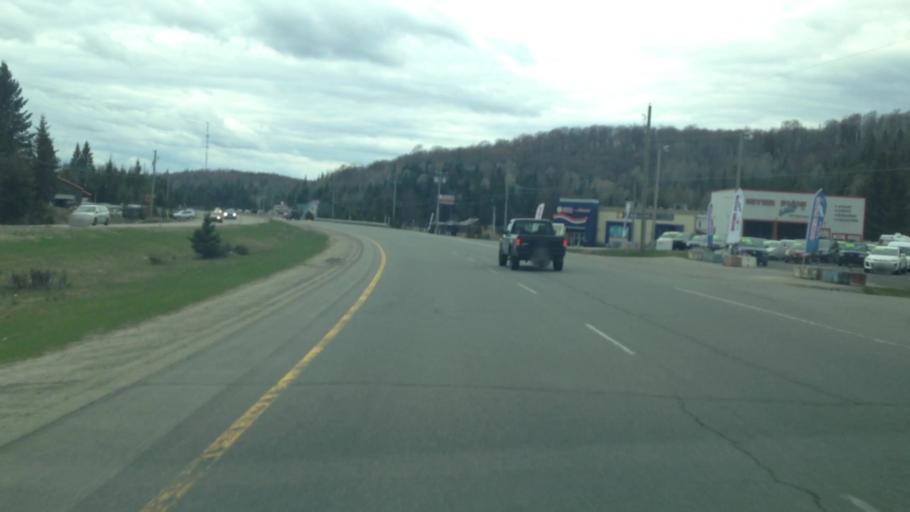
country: CA
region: Quebec
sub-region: Laurentides
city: Sainte-Agathe-des-Monts
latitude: 46.0777
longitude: -74.3140
